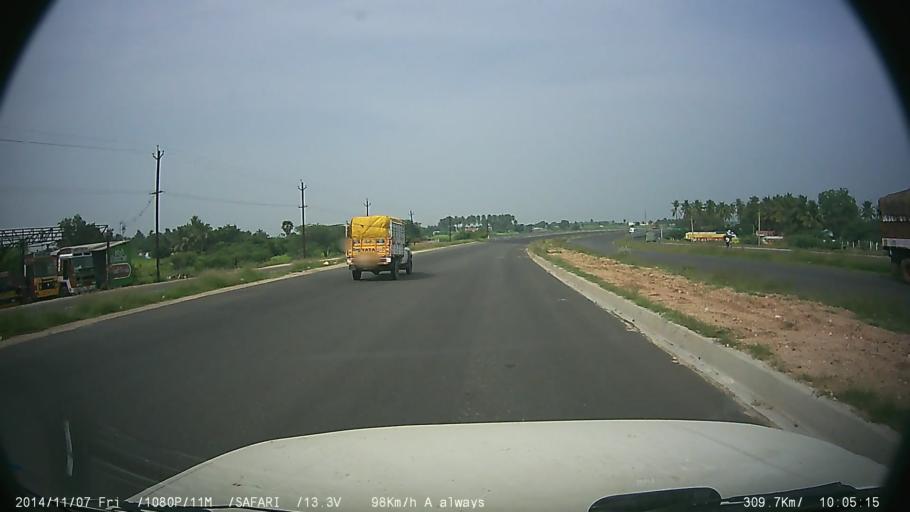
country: IN
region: Tamil Nadu
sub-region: Tiruppur
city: Uttukkuli
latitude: 11.2070
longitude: 77.3736
